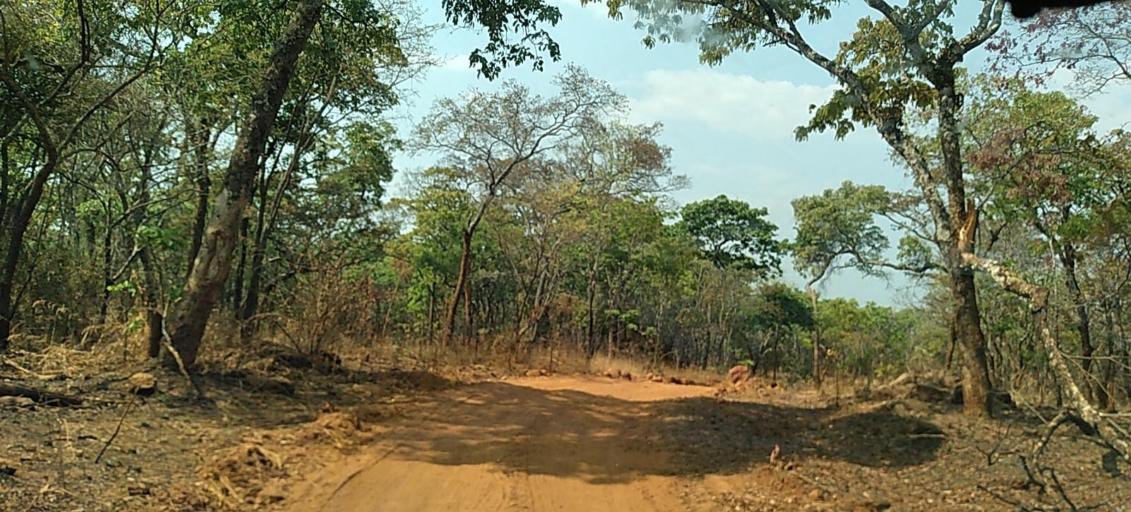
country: ZM
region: North-Western
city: Kasempa
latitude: -13.3128
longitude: 26.0592
